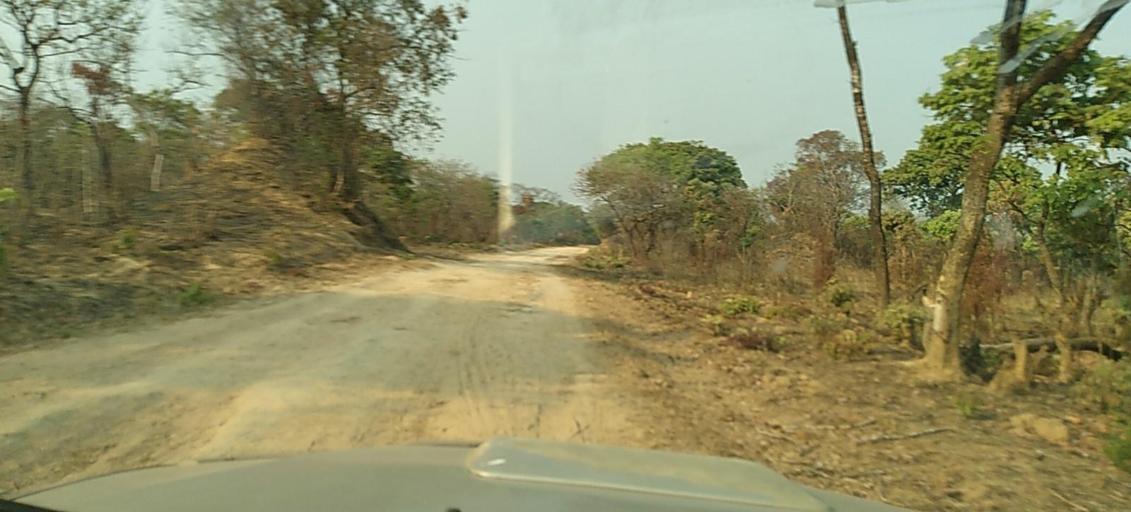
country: ZM
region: North-Western
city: Kasempa
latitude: -13.2696
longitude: 26.5591
